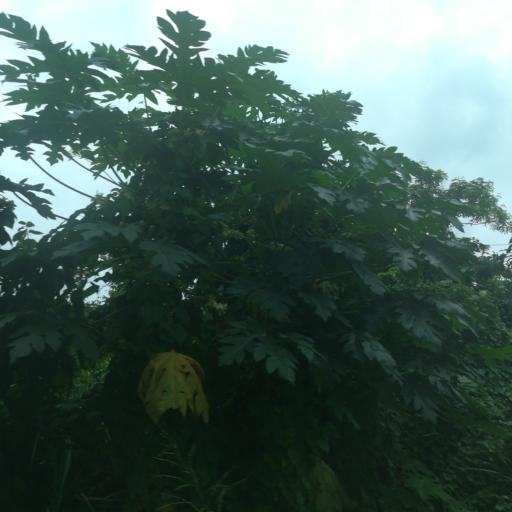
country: NG
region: Ogun
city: Odogbolu
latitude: 6.6658
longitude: 3.7101
